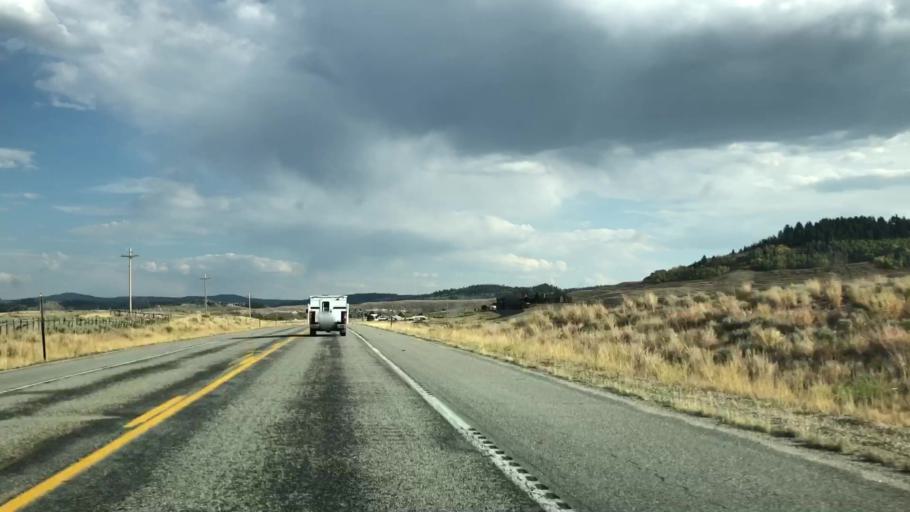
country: US
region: Wyoming
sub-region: Teton County
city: Hoback
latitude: 43.1720
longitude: -110.3796
